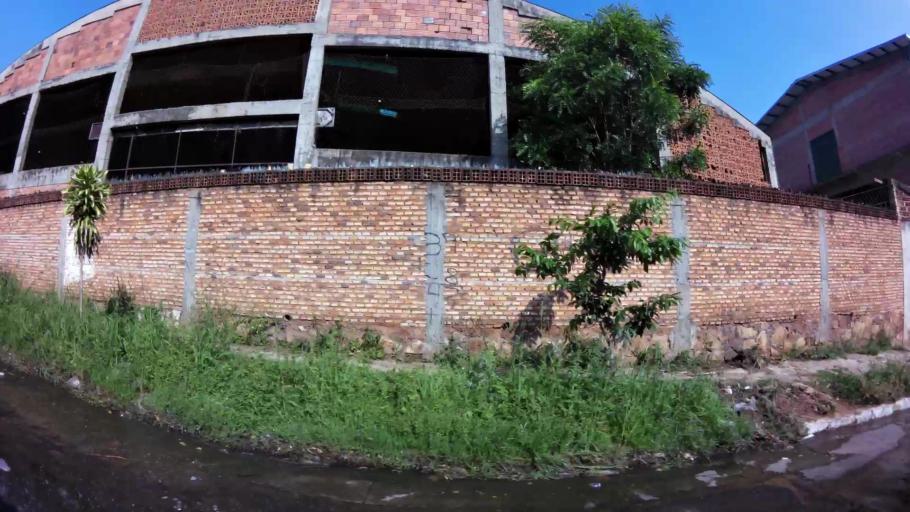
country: PY
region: Asuncion
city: Asuncion
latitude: -25.3090
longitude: -57.6238
